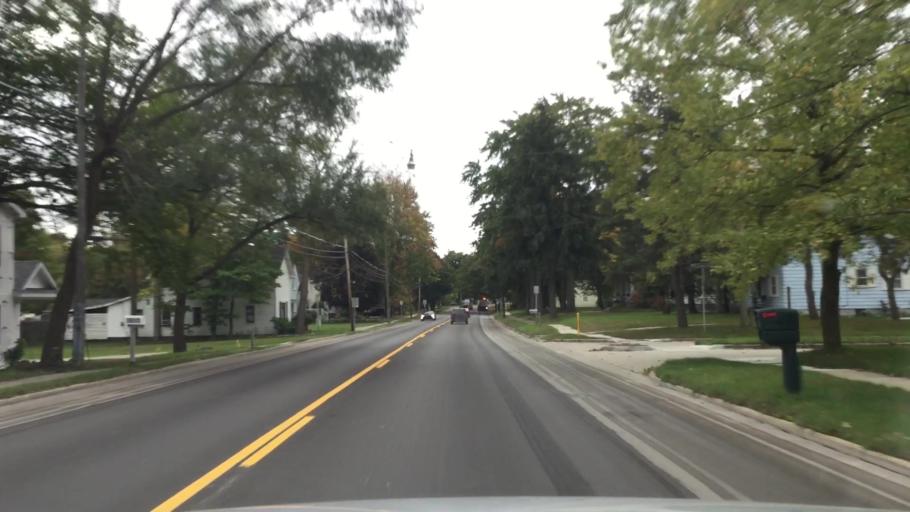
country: US
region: Michigan
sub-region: Macomb County
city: Richmond
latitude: 42.8193
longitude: -82.7604
